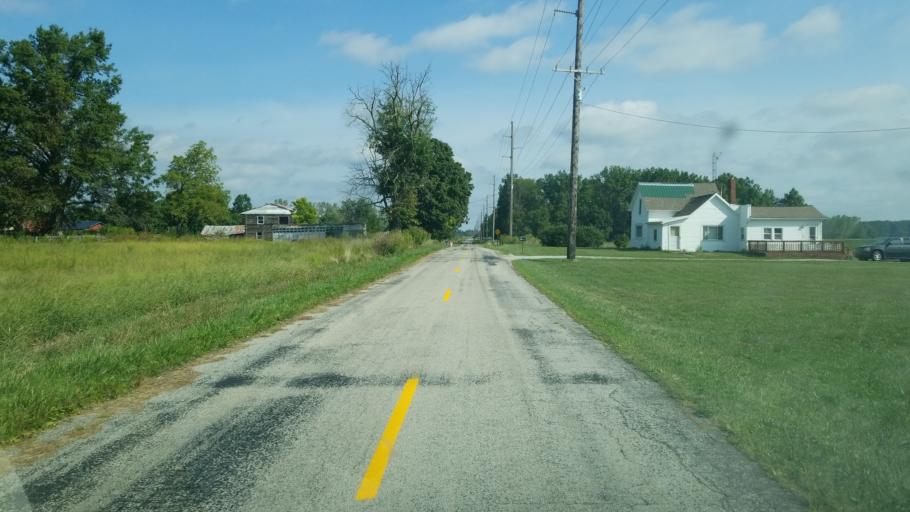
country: US
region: Ohio
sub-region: Wyandot County
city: Upper Sandusky
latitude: 40.6721
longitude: -83.3241
